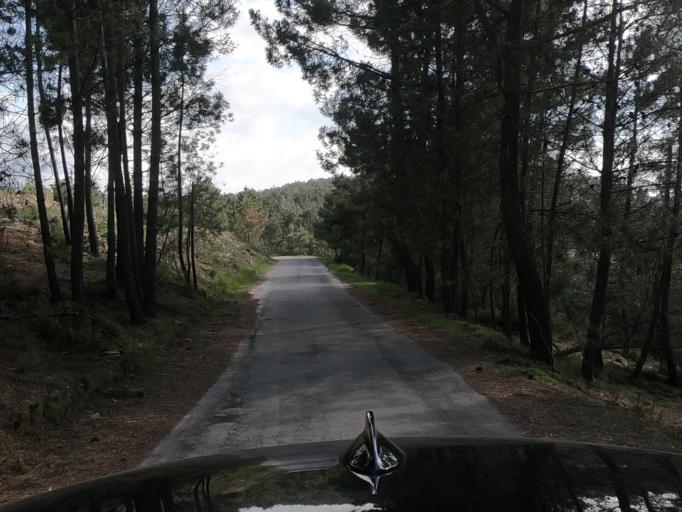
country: PT
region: Vila Real
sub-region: Sabrosa
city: Vilela
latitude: 41.2465
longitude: -7.6607
